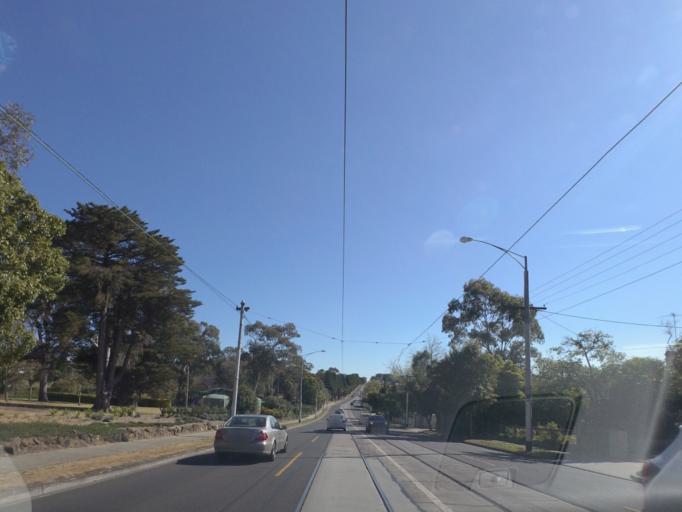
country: AU
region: Victoria
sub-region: Boroondara
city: Kew East
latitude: -37.8003
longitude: 145.0484
